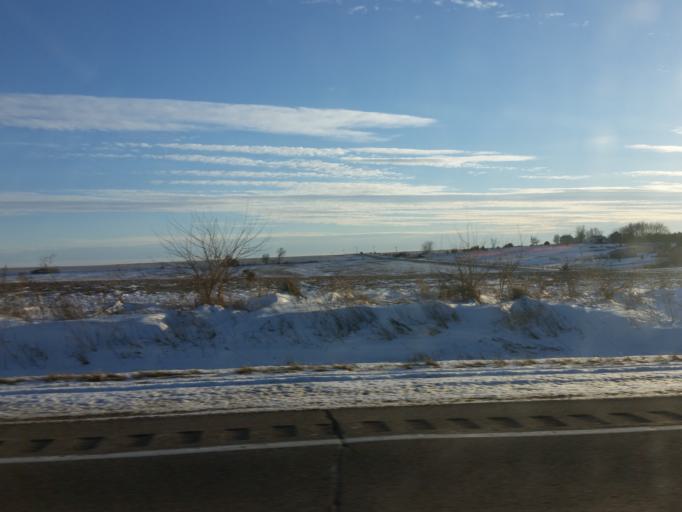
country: US
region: Iowa
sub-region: Butler County
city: Allison
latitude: 42.7450
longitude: -92.8478
